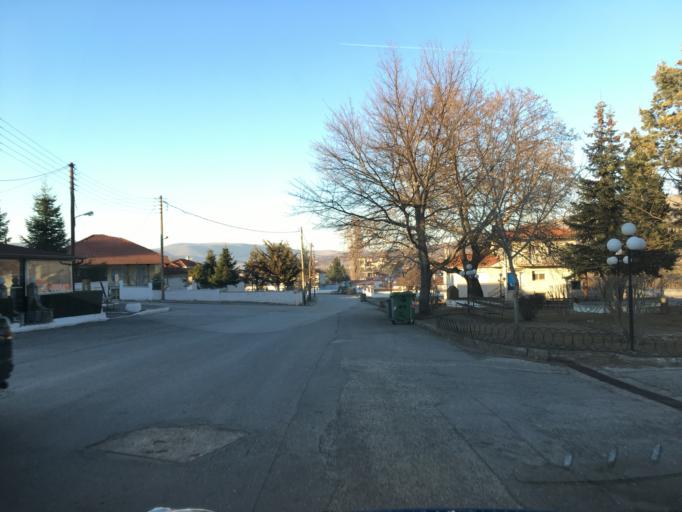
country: GR
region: West Macedonia
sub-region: Nomos Kozanis
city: Kozani
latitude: 40.2859
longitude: 21.7332
